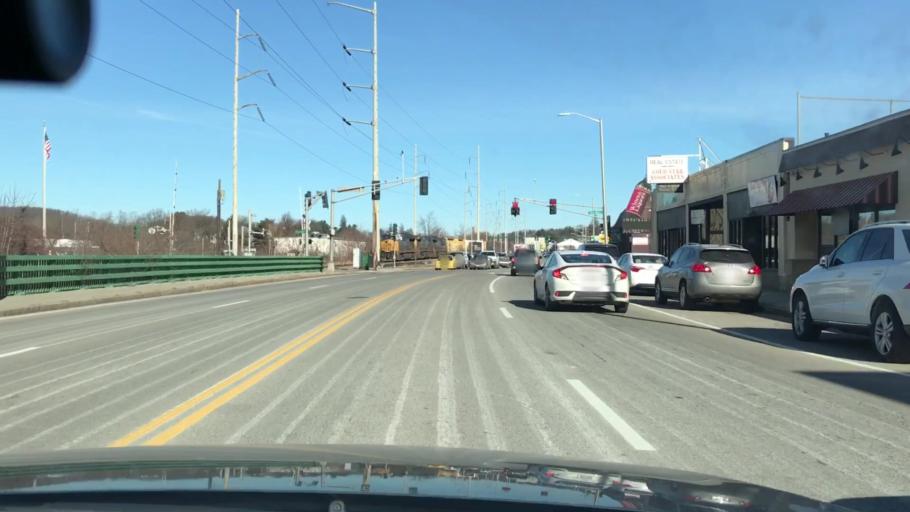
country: US
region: Massachusetts
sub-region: Worcester County
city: Worcester
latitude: 42.3045
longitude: -71.8009
